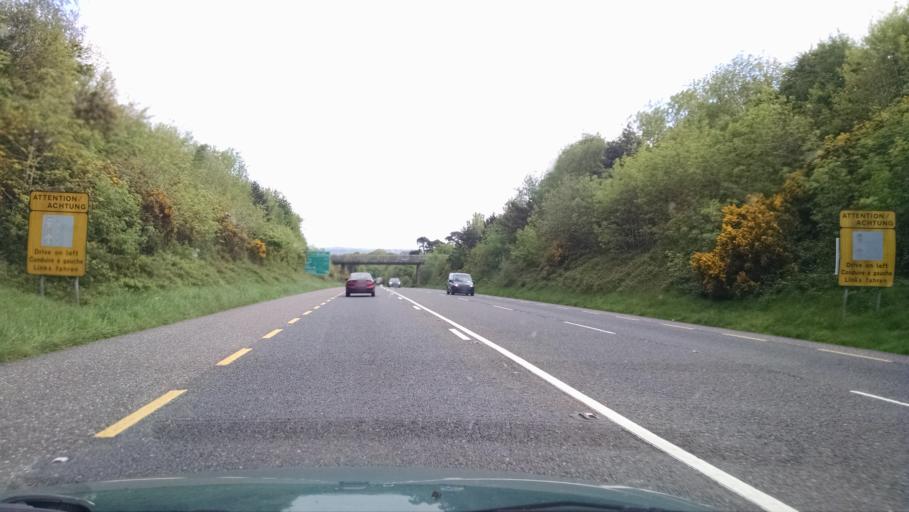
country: IE
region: Munster
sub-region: County Cork
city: Carrigaline
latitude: 51.8650
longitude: -8.4169
